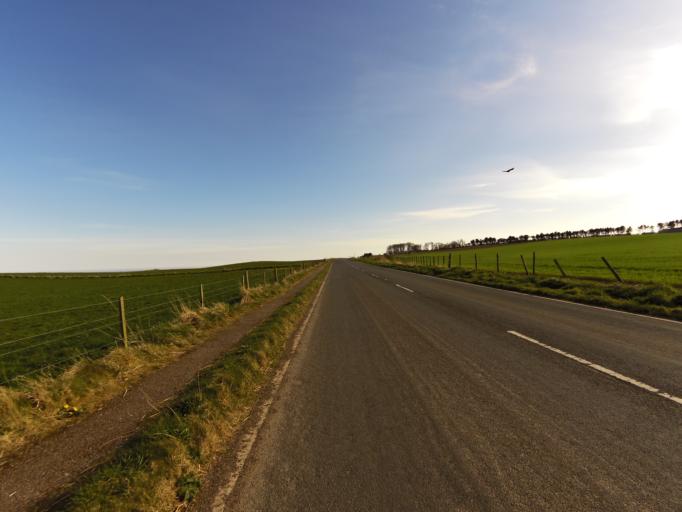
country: GB
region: Scotland
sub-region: Aberdeenshire
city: Stonehaven
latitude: 56.9502
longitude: -2.2051
